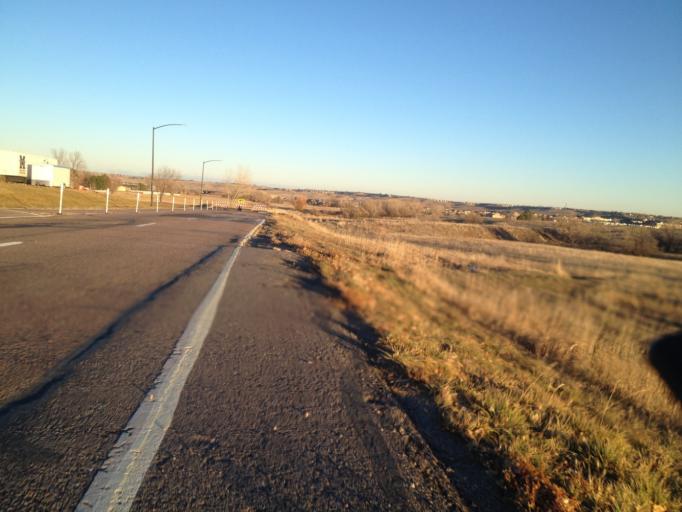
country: US
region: Colorado
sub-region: Boulder County
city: Superior
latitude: 39.9507
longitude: -105.1405
